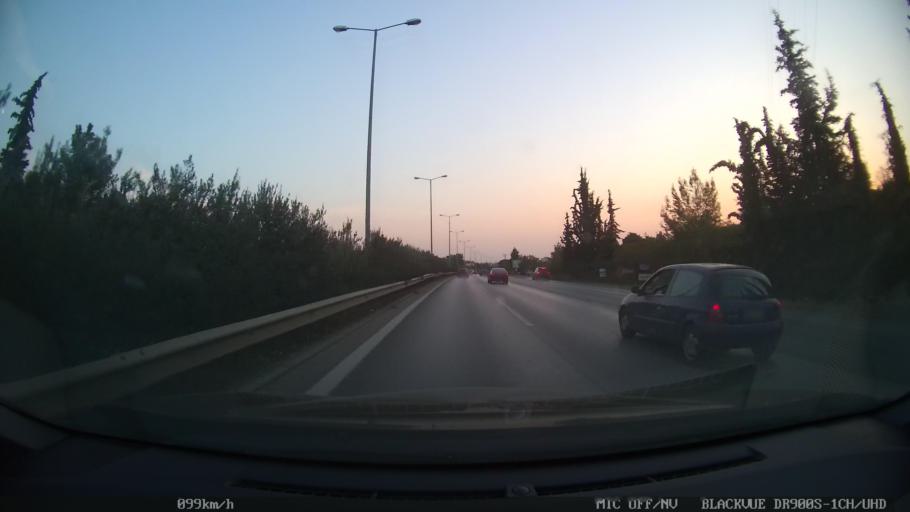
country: GR
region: Central Macedonia
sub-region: Nomos Thessalonikis
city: Pylaia
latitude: 40.5981
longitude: 22.9967
